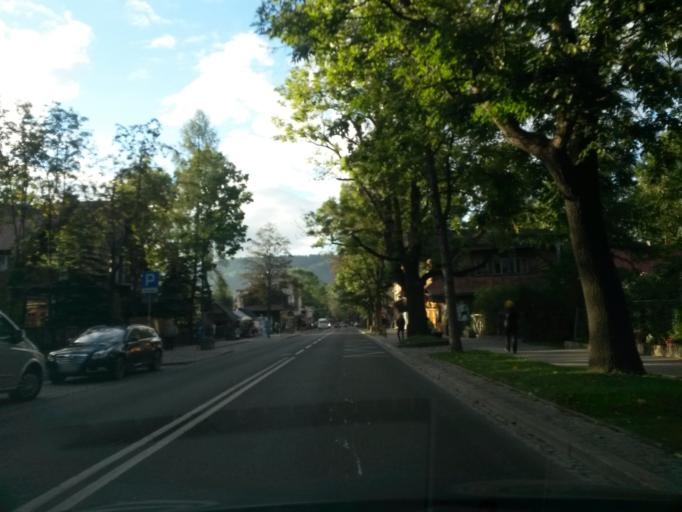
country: PL
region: Lesser Poland Voivodeship
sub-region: Powiat tatrzanski
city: Zakopane
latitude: 49.2902
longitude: 19.9629
